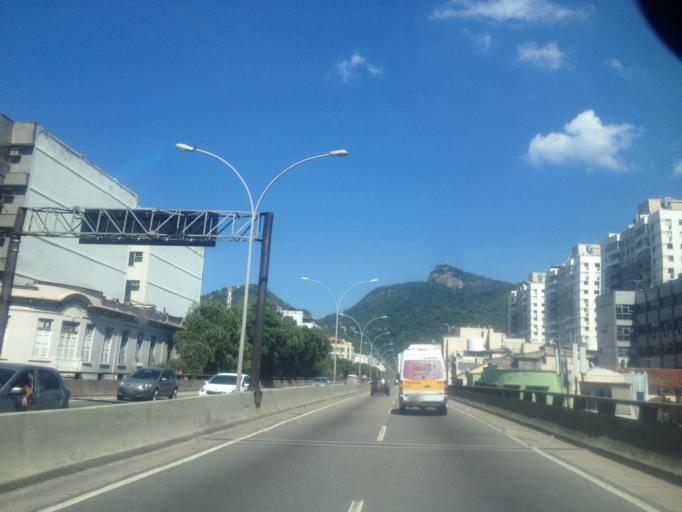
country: BR
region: Rio de Janeiro
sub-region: Rio De Janeiro
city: Rio de Janeiro
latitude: -22.9182
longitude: -43.2100
